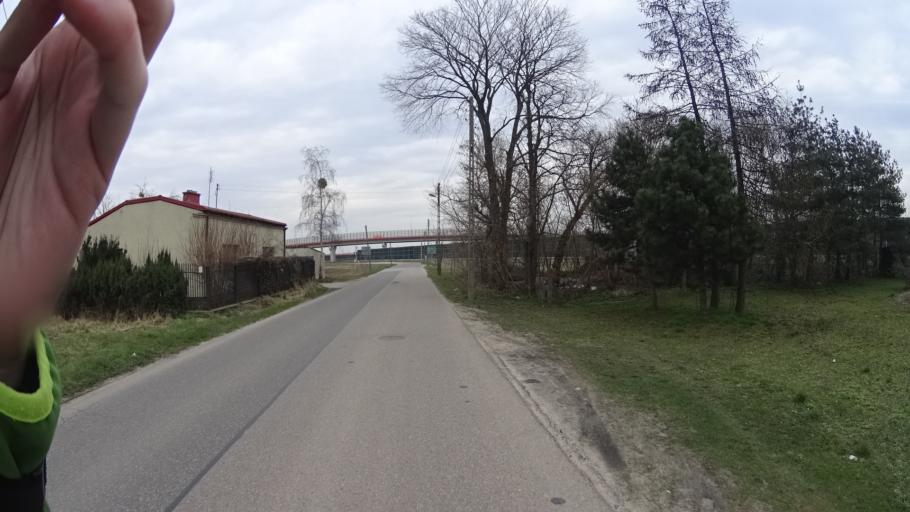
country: PL
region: Masovian Voivodeship
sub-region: Powiat pruszkowski
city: Piastow
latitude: 52.2014
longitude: 20.8390
